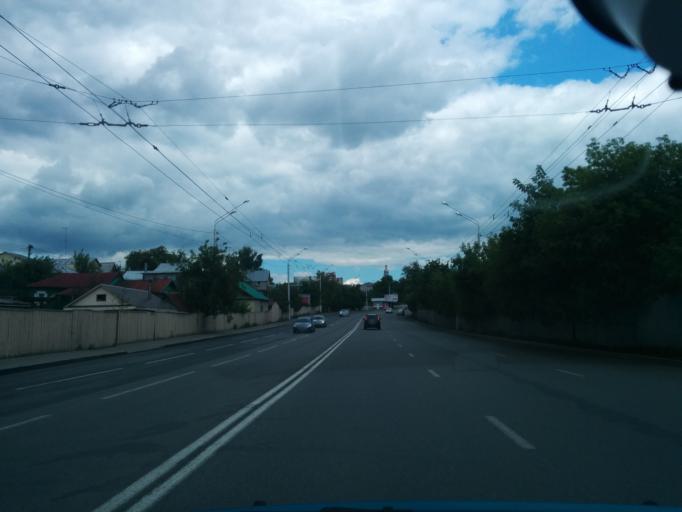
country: RU
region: Bashkortostan
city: Ufa
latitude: 54.7216
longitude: 55.9763
